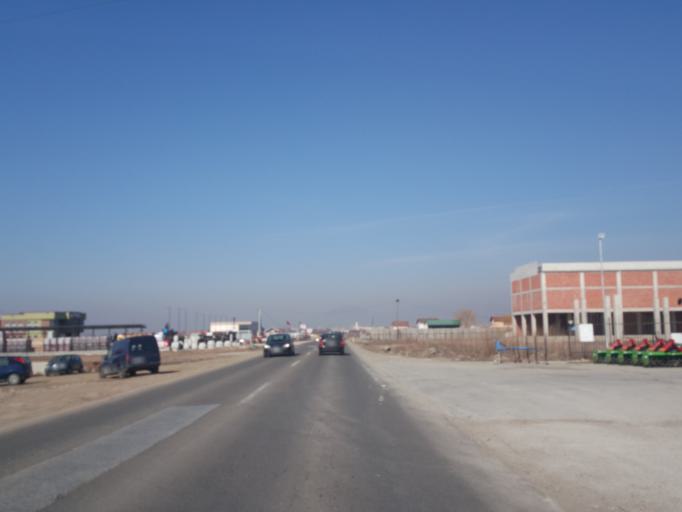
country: XK
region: Mitrovica
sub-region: Vushtrri
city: Vushtrri
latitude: 42.7903
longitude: 21.0049
